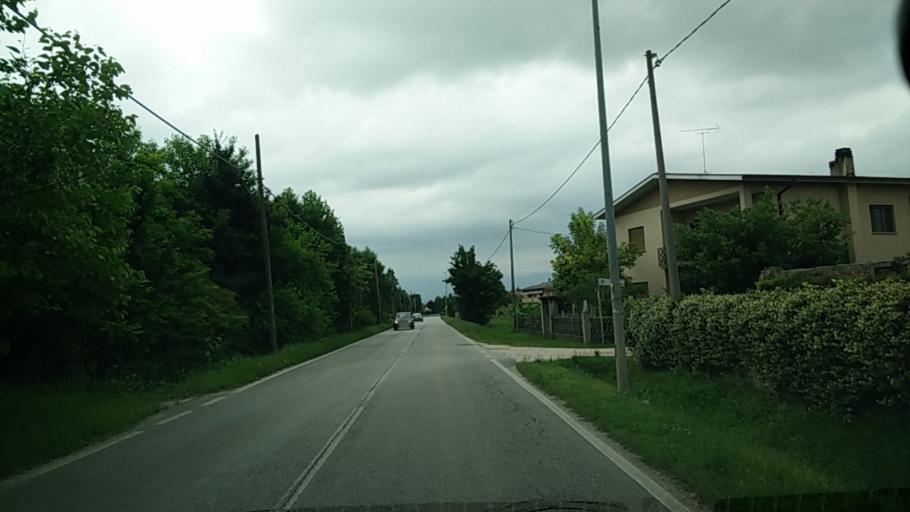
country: IT
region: Veneto
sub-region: Provincia di Treviso
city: Mareno di Piave
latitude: 45.8518
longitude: 12.3421
